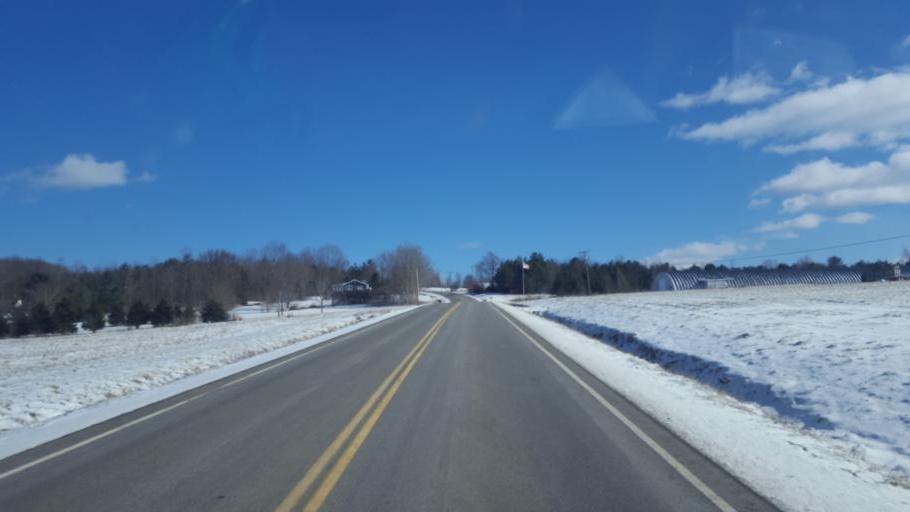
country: US
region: New York
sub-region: Allegany County
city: Friendship
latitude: 42.2037
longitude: -78.1170
